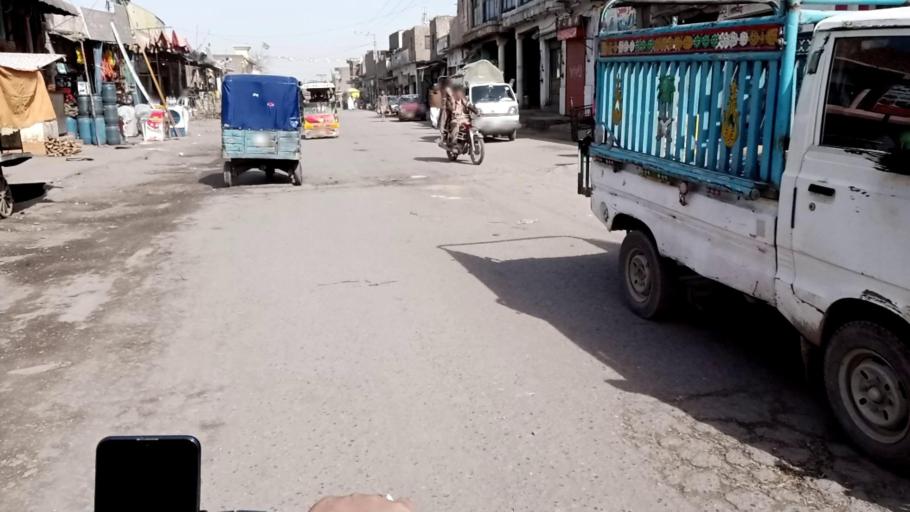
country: PK
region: Khyber Pakhtunkhwa
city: Peshawar
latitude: 33.9821
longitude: 71.6338
